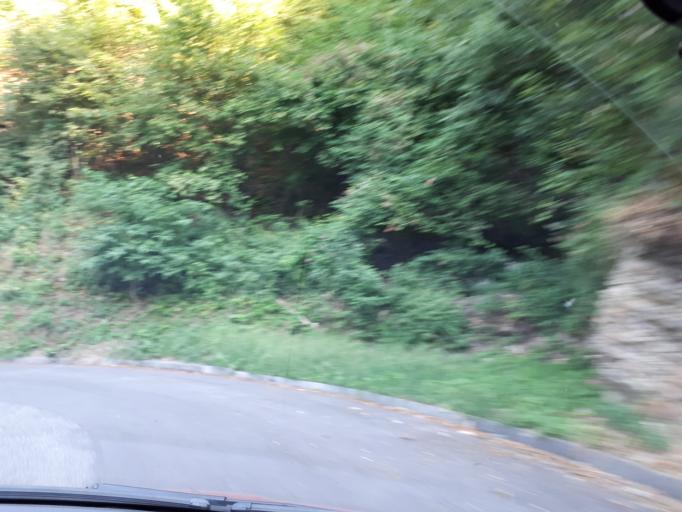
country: IT
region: Lombardy
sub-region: Provincia di Varese
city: Veddasca
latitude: 46.0967
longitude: 8.8281
